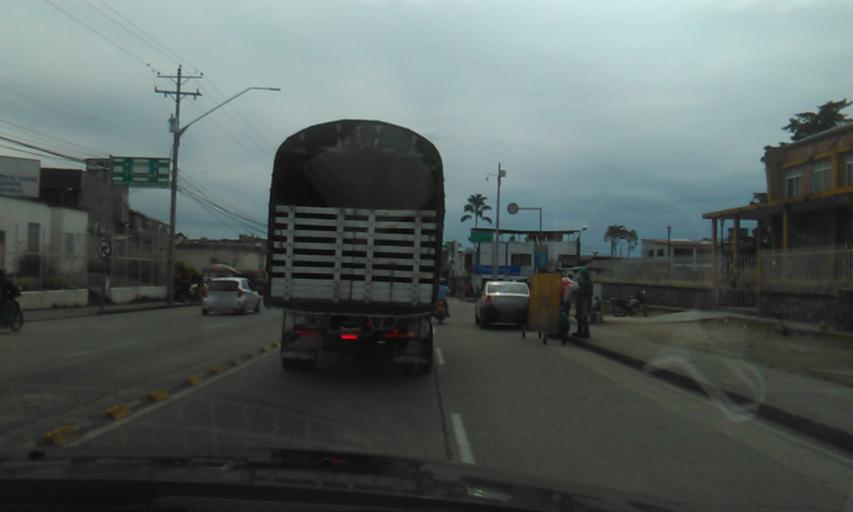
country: CO
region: Quindio
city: Armenia
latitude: 4.5222
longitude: -75.6868
